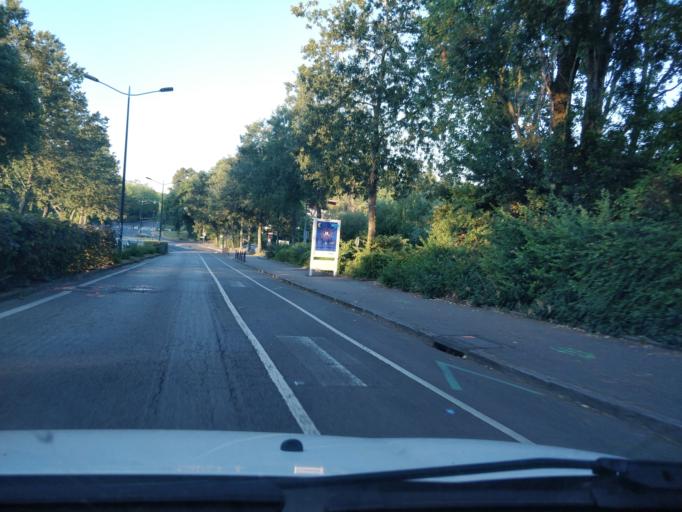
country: FR
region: Pays de la Loire
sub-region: Departement de la Loire-Atlantique
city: Nantes
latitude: 47.2479
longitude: -1.5551
